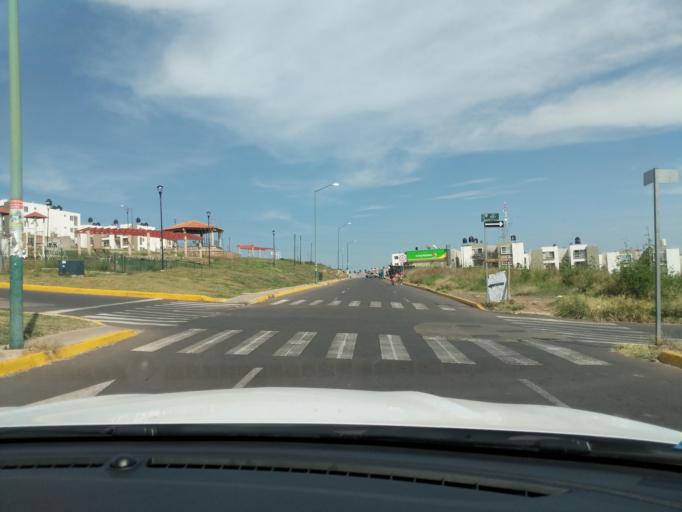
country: MX
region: Jalisco
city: San Jose del Castillo
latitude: 20.5207
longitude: -103.2223
